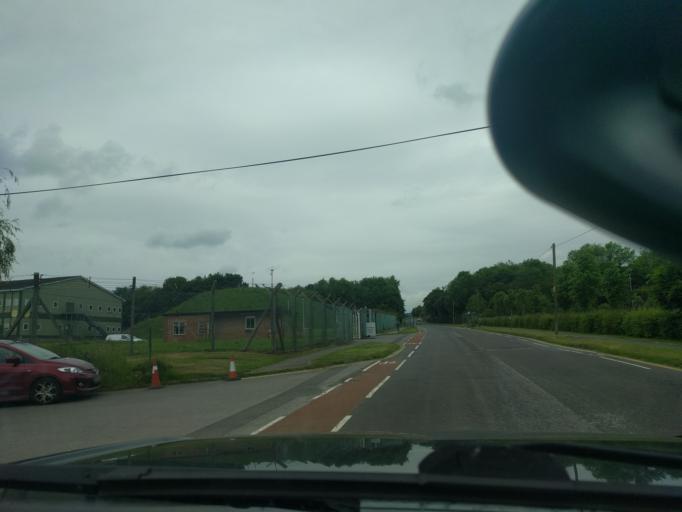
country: GB
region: England
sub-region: Wiltshire
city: Neston
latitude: 51.4206
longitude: -2.2169
